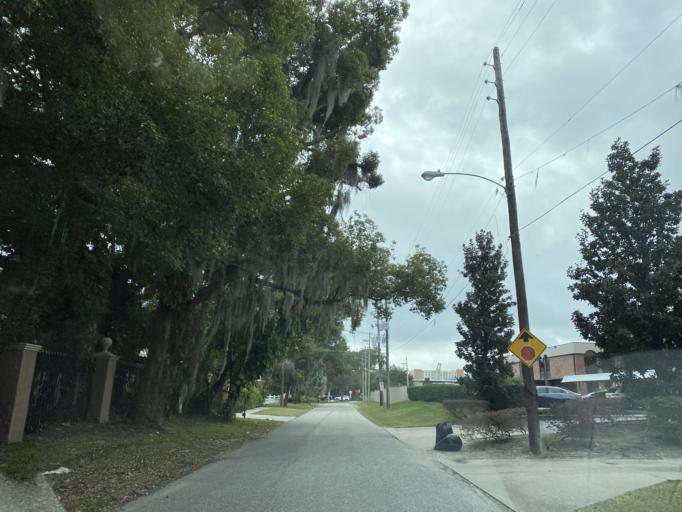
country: US
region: Florida
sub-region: Orange County
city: Orlando
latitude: 28.5537
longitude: -81.3862
